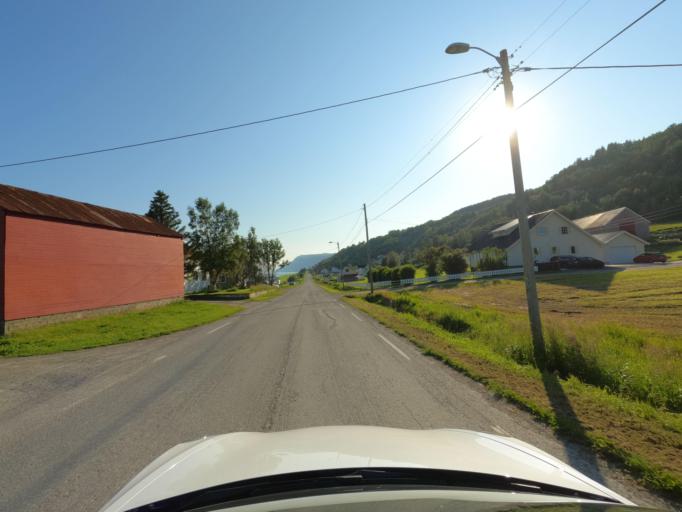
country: NO
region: Nordland
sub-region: Narvik
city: Bjerkvik
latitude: 68.5313
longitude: 17.4718
